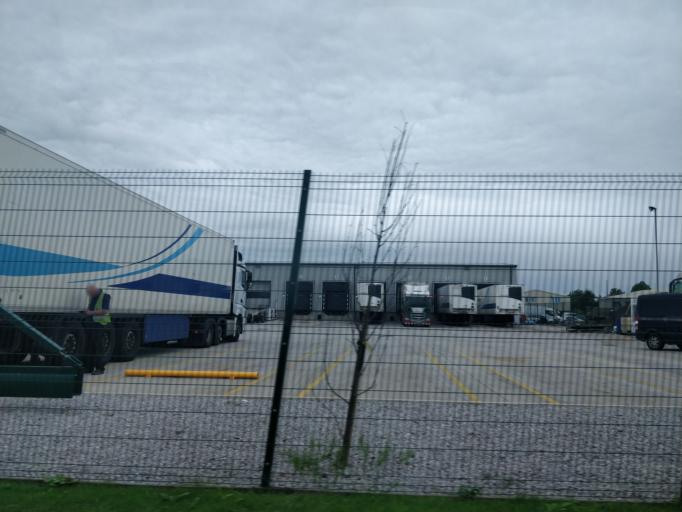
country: GB
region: England
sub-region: Lancashire
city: Ormskirk
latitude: 53.5962
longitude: -2.8620
